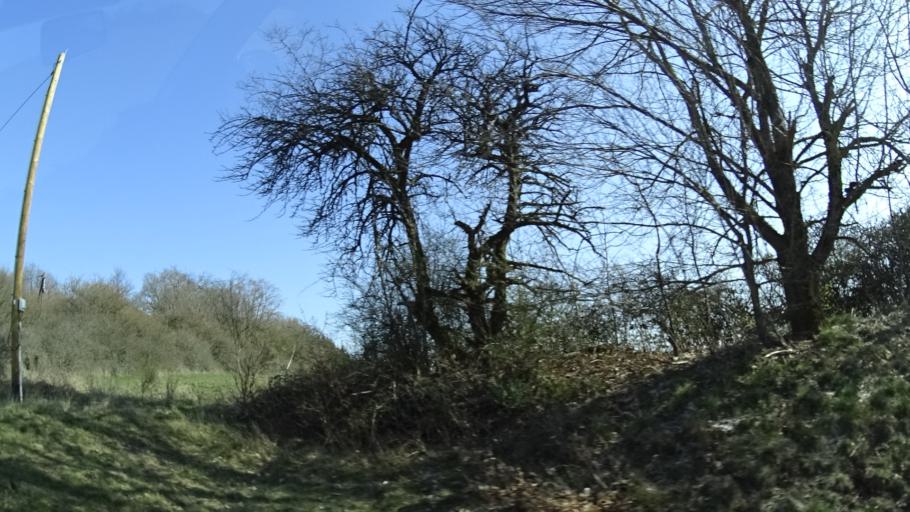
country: DE
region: Rheinland-Pfalz
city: Niederbrombach
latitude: 49.6846
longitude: 7.2599
